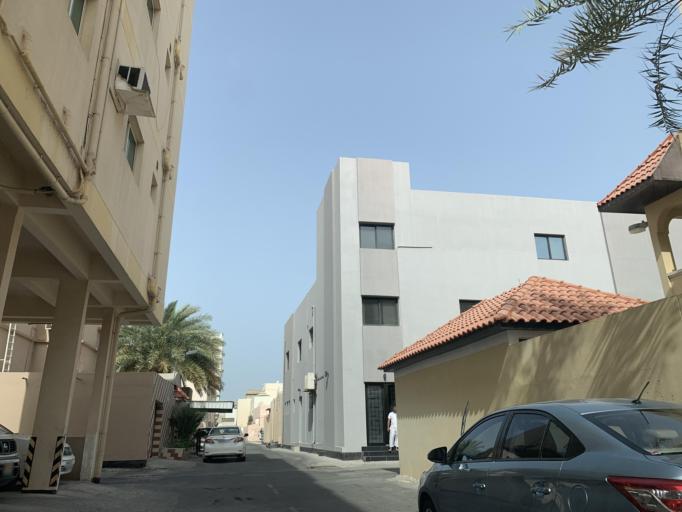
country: BH
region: Northern
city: Ar Rifa'
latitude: 26.1248
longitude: 50.5723
